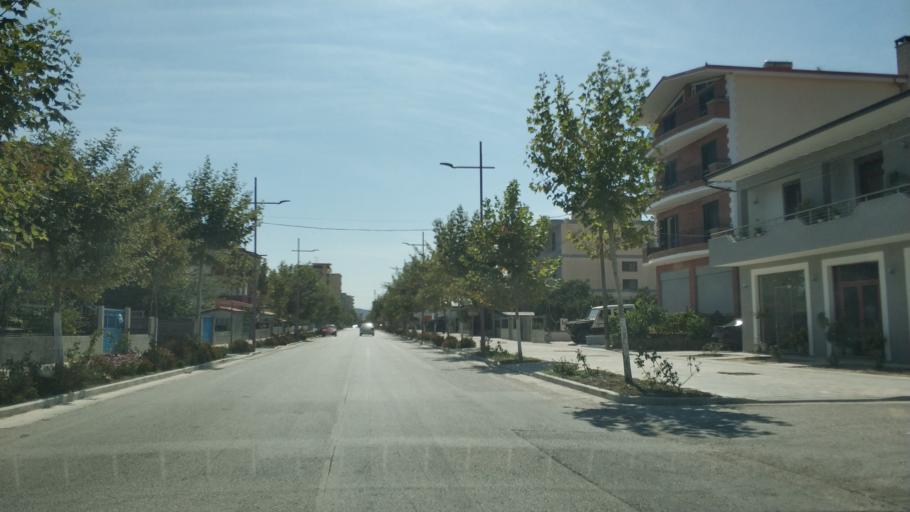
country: AL
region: Fier
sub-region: Rrethi i Lushnjes
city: Divjake
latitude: 41.0014
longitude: 19.5306
